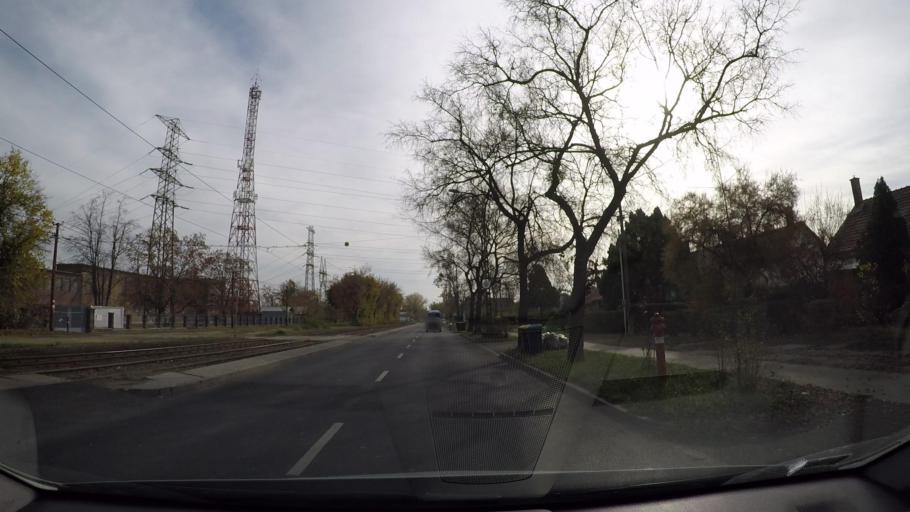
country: HU
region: Budapest
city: Budapest X. keruelet
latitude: 47.4756
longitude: 19.1681
